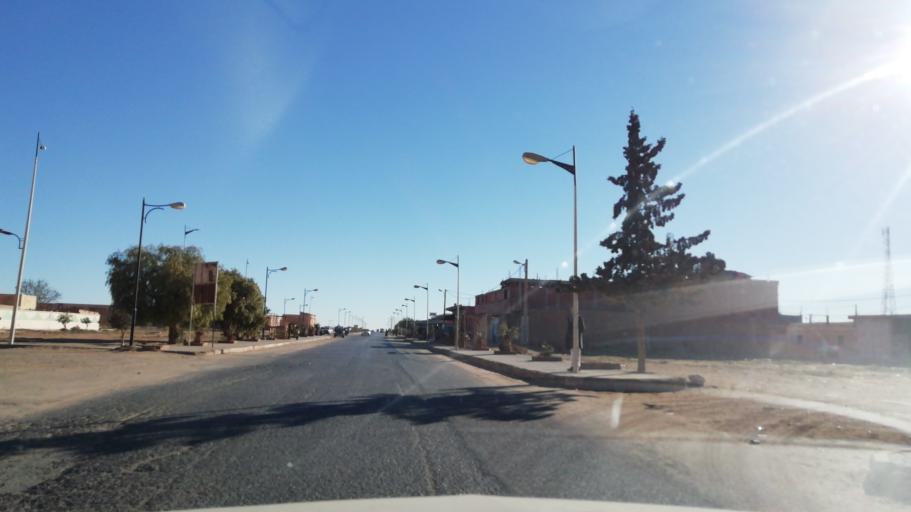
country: DZ
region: El Bayadh
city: El Bayadh
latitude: 33.8526
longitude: 0.6426
